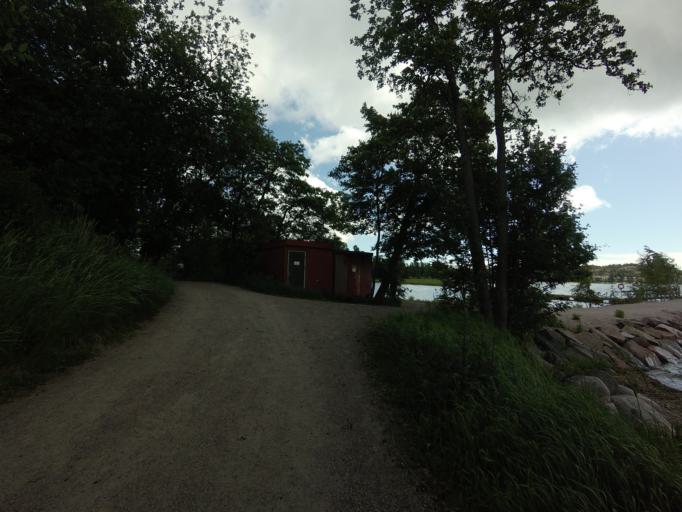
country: FI
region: Uusimaa
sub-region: Helsinki
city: Espoo
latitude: 60.1349
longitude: 24.6493
